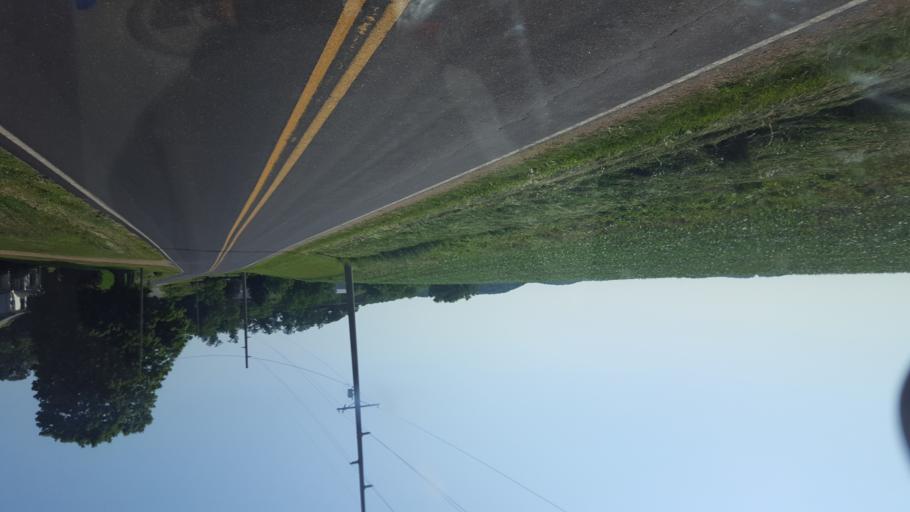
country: US
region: Wisconsin
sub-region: Vernon County
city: Hillsboro
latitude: 43.6662
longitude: -90.3496
